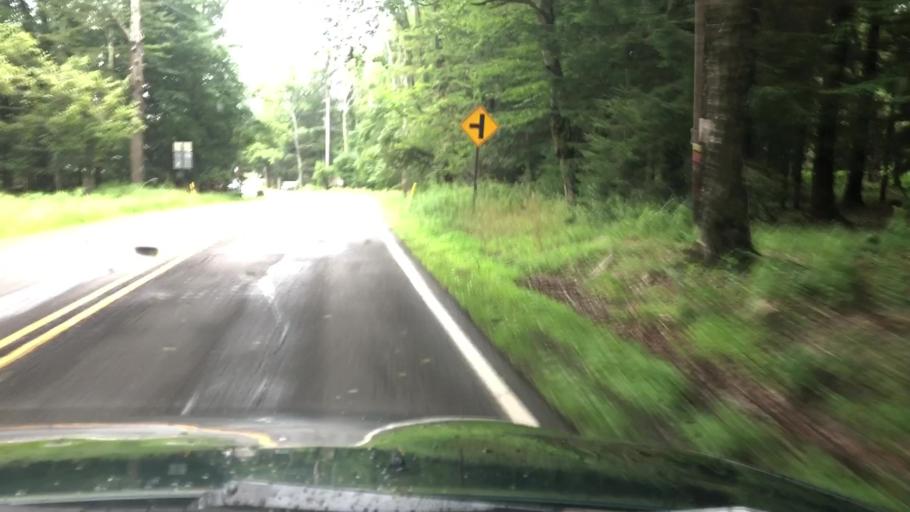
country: US
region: Pennsylvania
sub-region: Monroe County
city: Mountainhome
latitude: 41.3084
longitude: -75.2109
